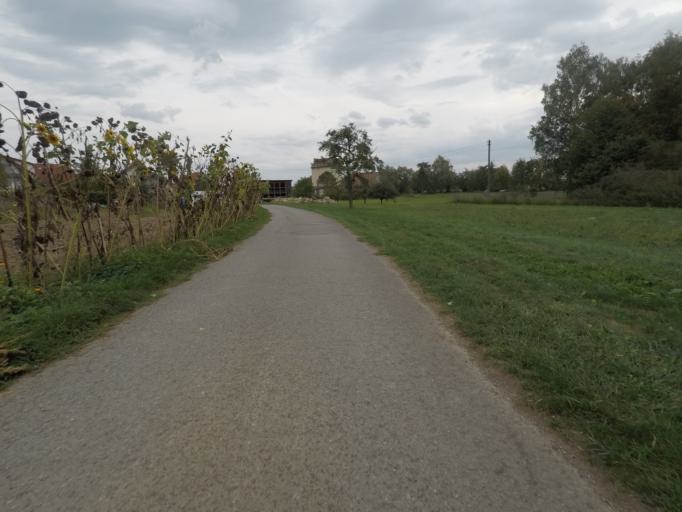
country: DE
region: Baden-Wuerttemberg
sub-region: Regierungsbezirk Stuttgart
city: Herrenberg
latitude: 48.5722
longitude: 8.8732
